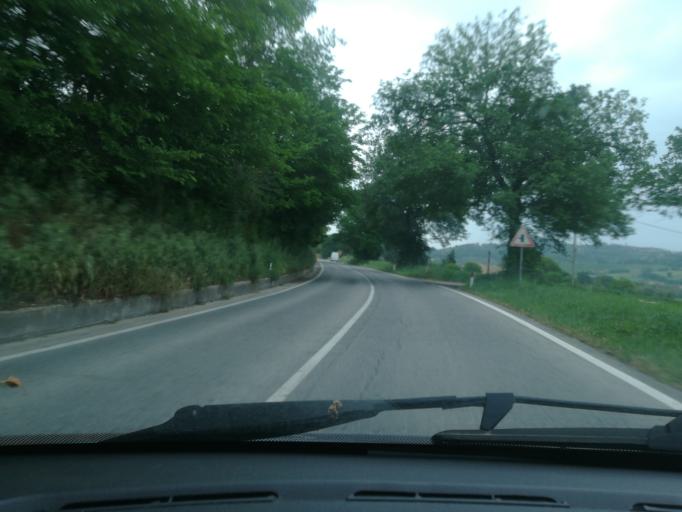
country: IT
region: The Marches
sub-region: Provincia di Macerata
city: Passo di Treia
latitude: 43.2779
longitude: 13.3087
